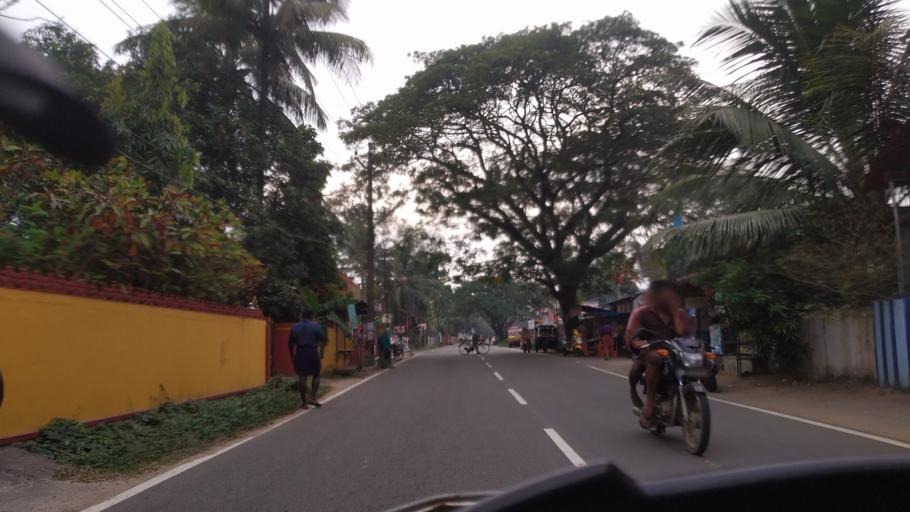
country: IN
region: Kerala
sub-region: Ernakulam
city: Elur
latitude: 10.1497
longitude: 76.2552
